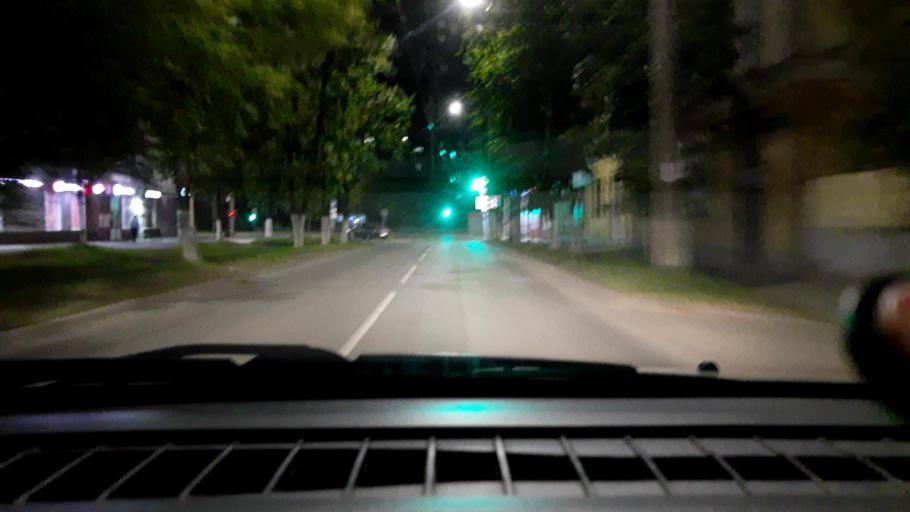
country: RU
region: Nizjnij Novgorod
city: Dzerzhinsk
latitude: 56.2360
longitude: 43.4791
